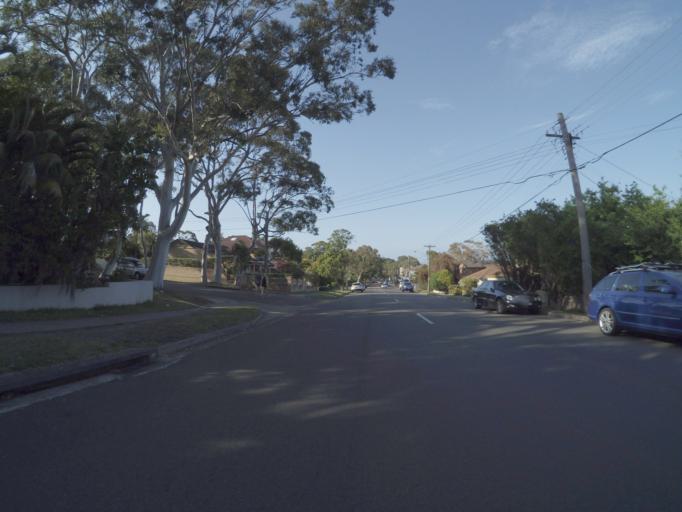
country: AU
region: New South Wales
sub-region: Sutherland Shire
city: Cronulla
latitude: -34.0538
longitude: 151.1403
